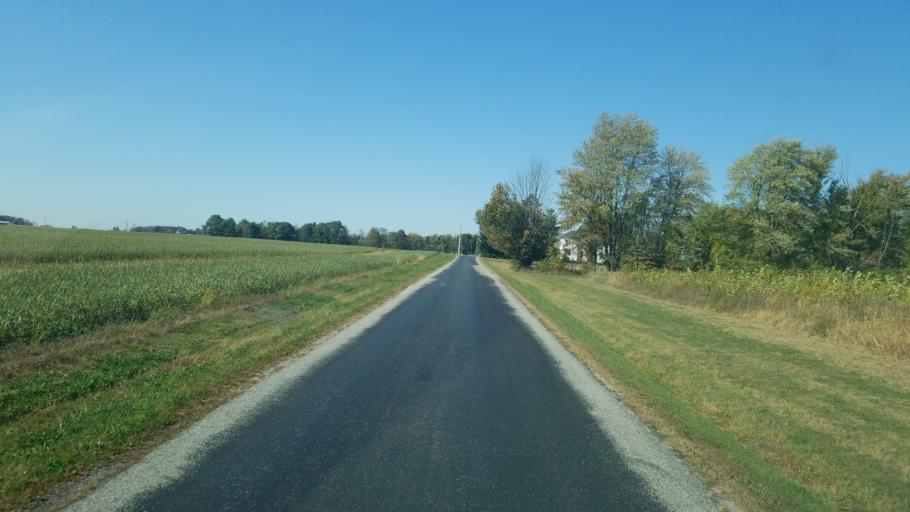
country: US
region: Ohio
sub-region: Marion County
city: Prospect
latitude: 40.4698
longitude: -83.1035
